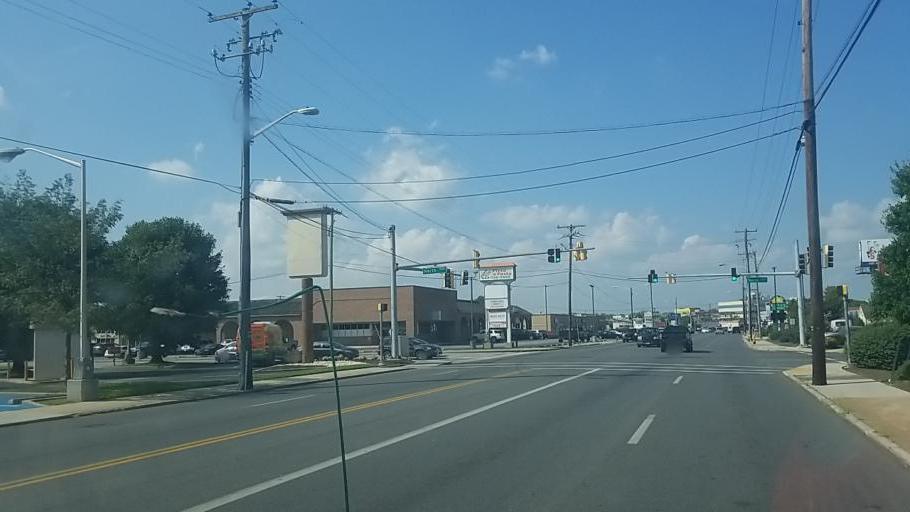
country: US
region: Maryland
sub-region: Wicomico County
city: Salisbury
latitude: 38.3551
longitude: -75.6005
